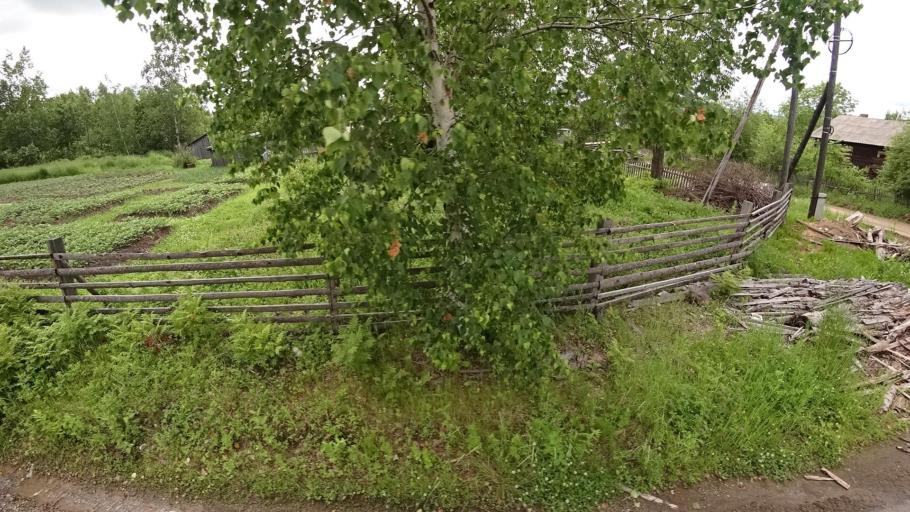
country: RU
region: Khabarovsk Krai
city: Litovko
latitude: 49.3629
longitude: 135.1745
